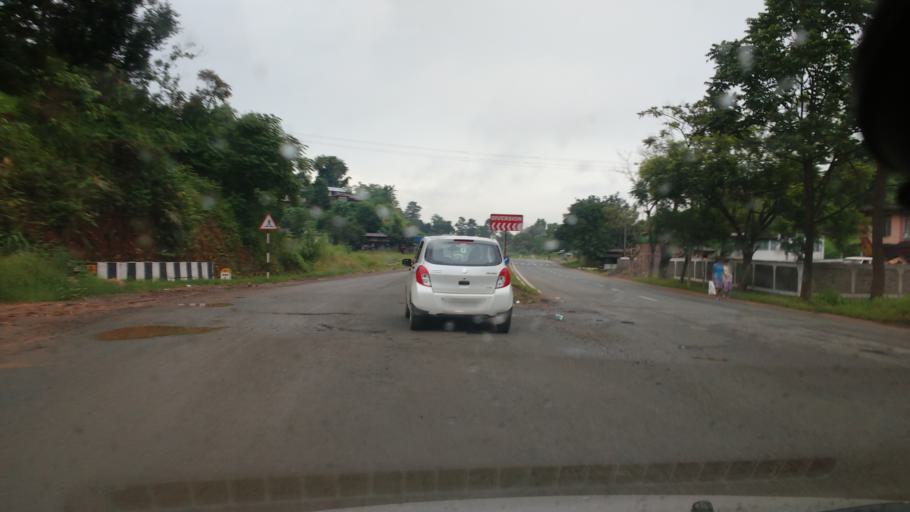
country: IN
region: Meghalaya
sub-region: Ri-Bhoi
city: Nongpoh
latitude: 25.7549
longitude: 91.8858
